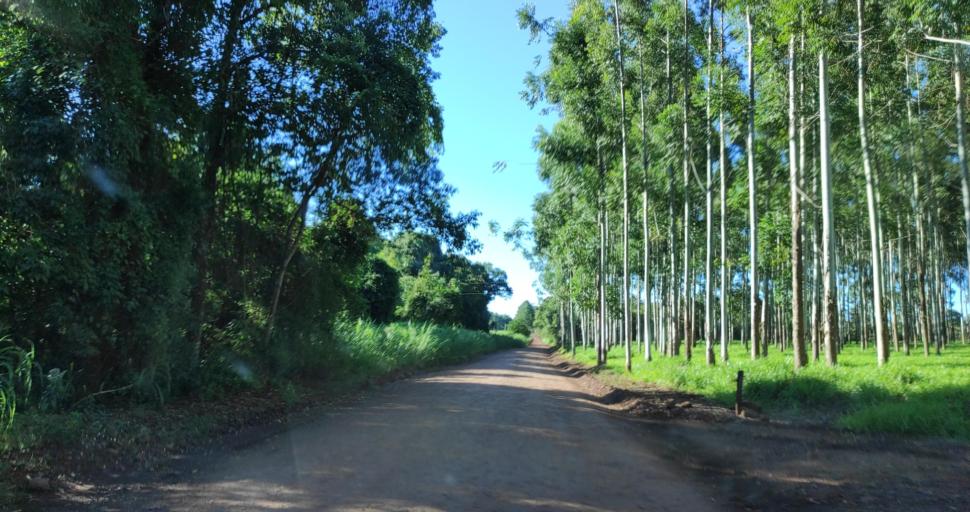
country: AR
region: Misiones
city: Garuhape
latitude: -26.8728
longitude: -54.9955
